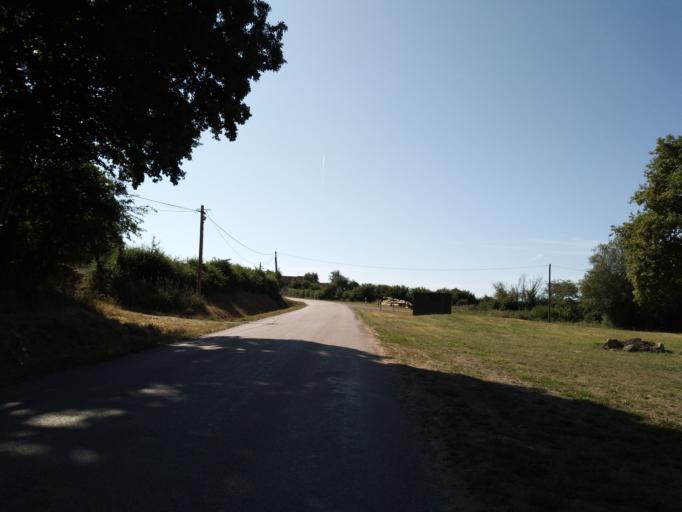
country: FR
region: Bourgogne
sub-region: Departement de la Cote-d'Or
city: Saulieu
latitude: 47.2897
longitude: 4.1352
